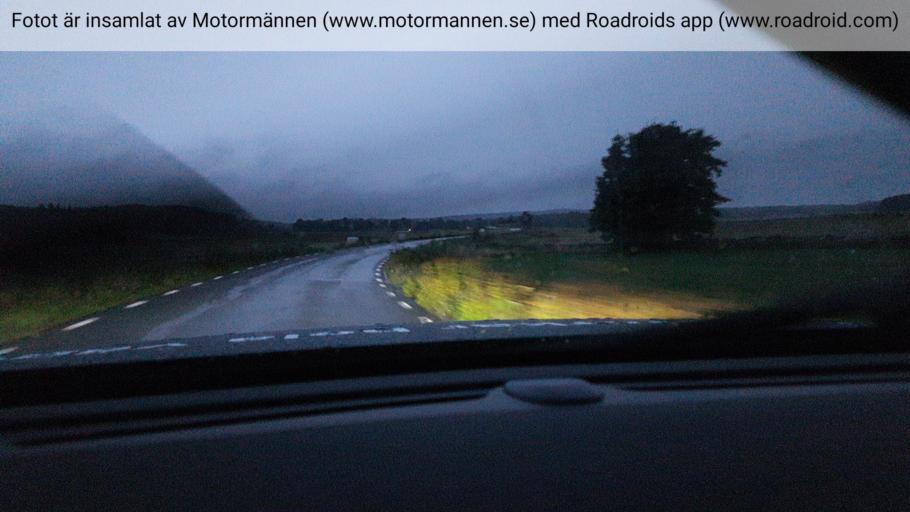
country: SE
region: Vaestra Goetaland
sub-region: Tidaholms Kommun
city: Tidaholm
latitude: 58.1721
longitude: 13.8193
